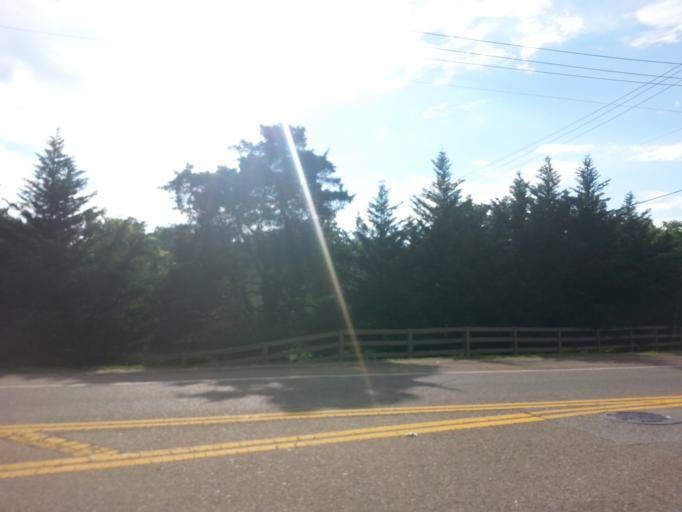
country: US
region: Tennessee
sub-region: Knox County
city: Knoxville
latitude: 35.9226
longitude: -83.9959
